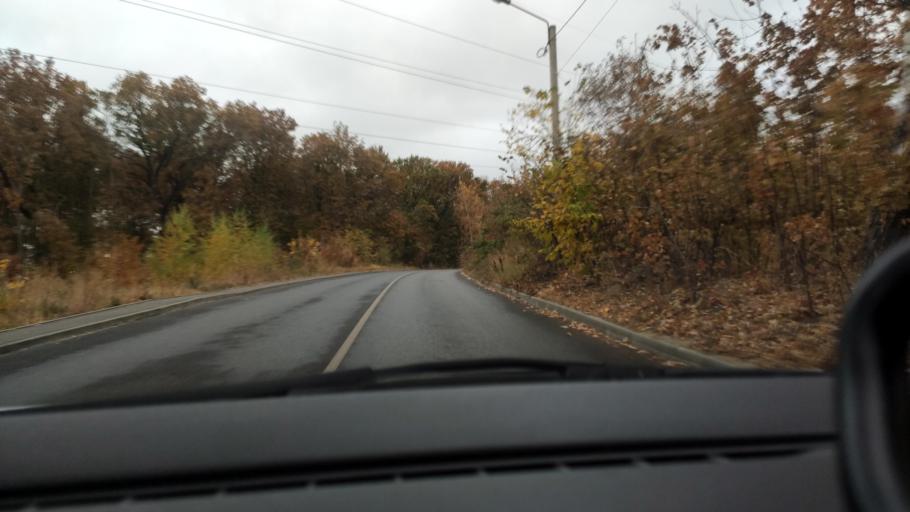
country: RU
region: Voronezj
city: Voronezh
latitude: 51.7175
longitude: 39.2362
